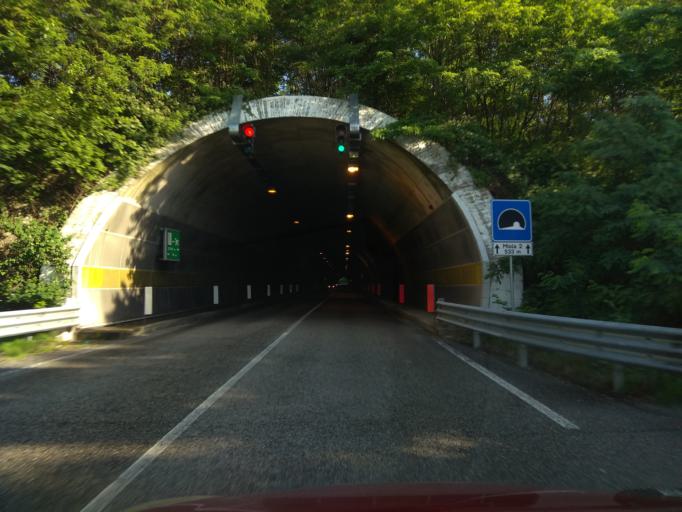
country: IT
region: Piedmont
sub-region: Provincia di Biella
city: Vallanzengo
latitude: 45.5995
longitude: 8.1685
